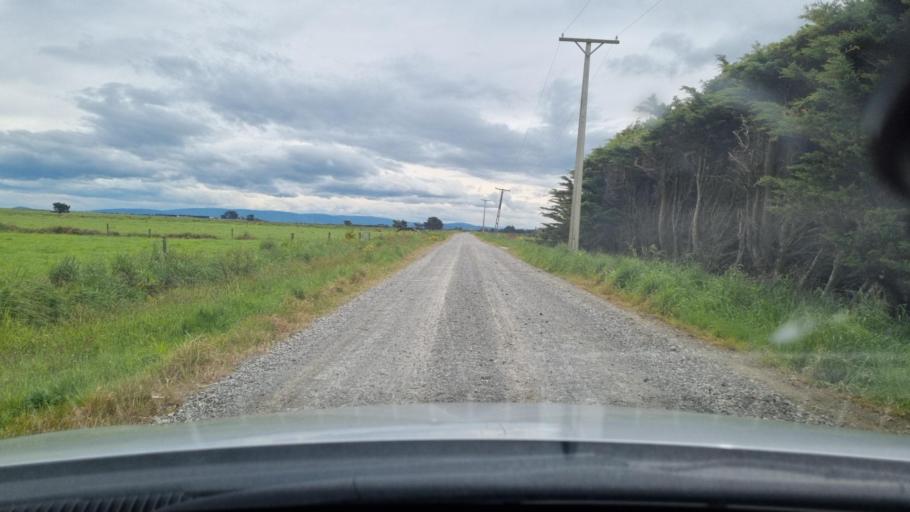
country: NZ
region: Southland
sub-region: Invercargill City
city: Invercargill
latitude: -46.4036
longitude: 168.2876
